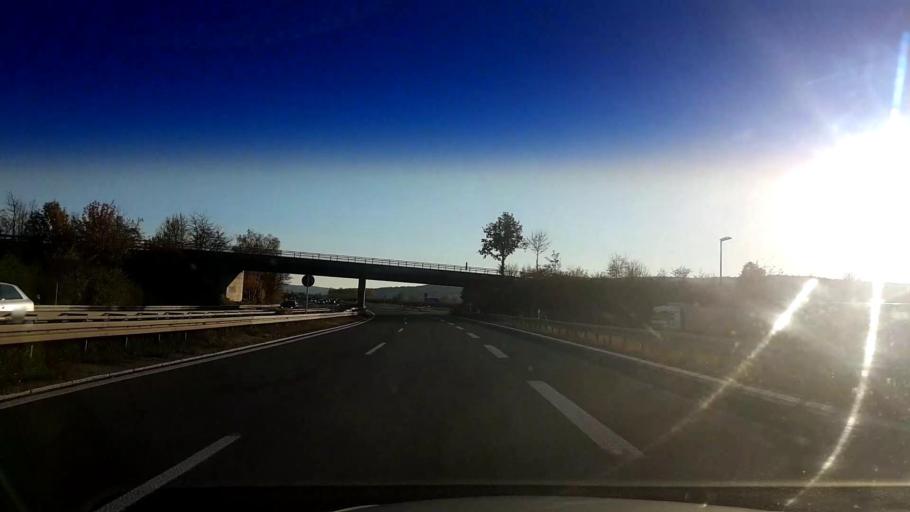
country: DE
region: Bavaria
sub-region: Upper Franconia
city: Breitengussbach
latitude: 49.9735
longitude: 10.8796
